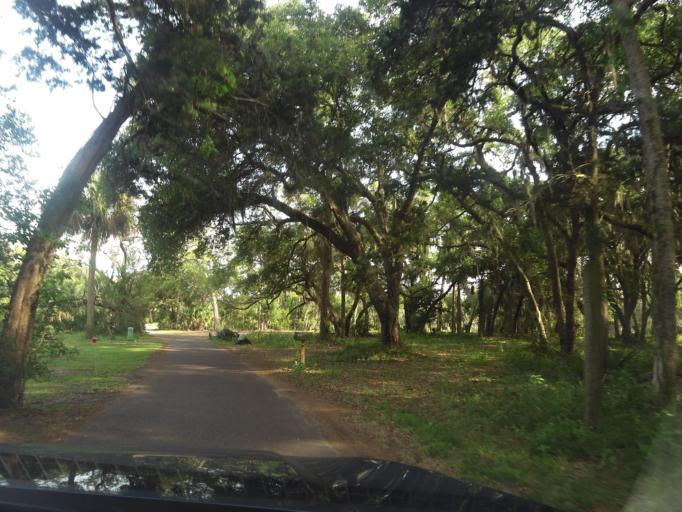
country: US
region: Florida
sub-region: Nassau County
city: Fernandina Beach
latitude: 30.5346
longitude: -81.4848
